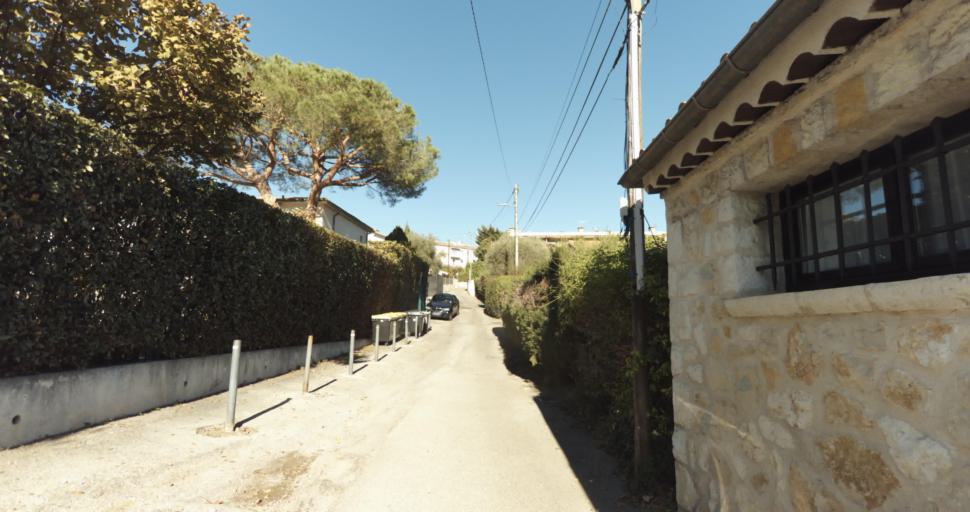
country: FR
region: Provence-Alpes-Cote d'Azur
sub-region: Departement des Alpes-Maritimes
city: Vence
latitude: 43.7180
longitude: 7.1167
